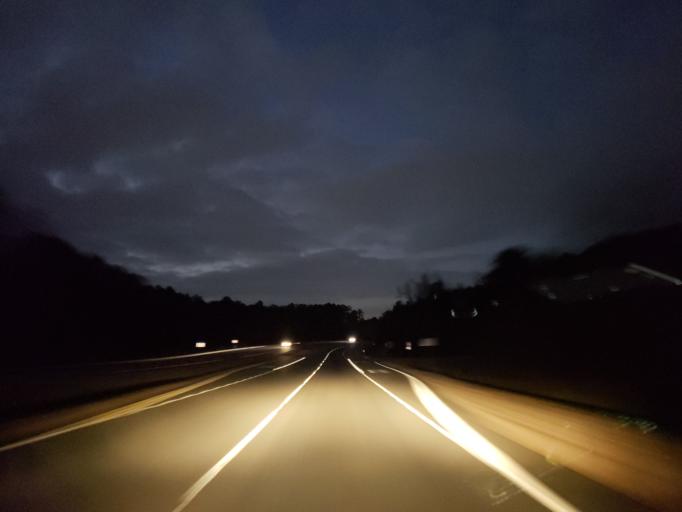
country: US
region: Georgia
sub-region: Polk County
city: Rockmart
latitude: 33.9894
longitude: -85.0224
